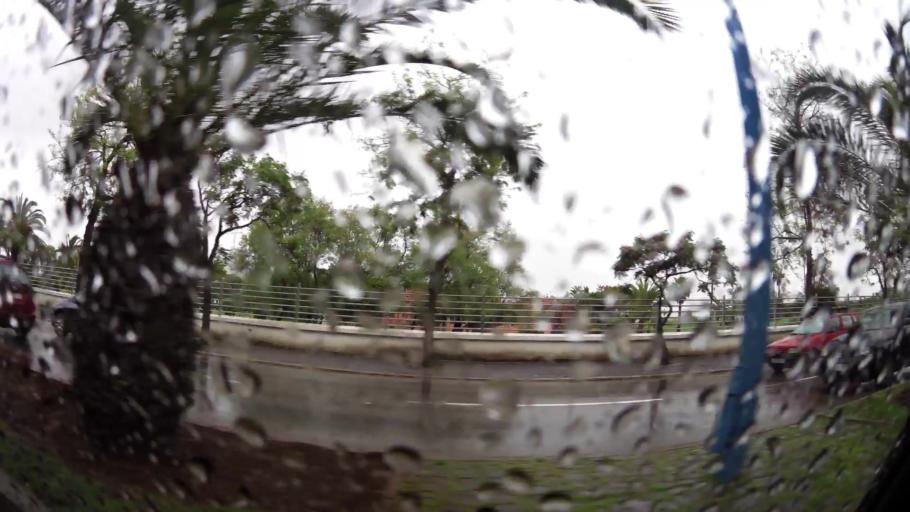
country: MA
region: Grand Casablanca
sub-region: Casablanca
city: Casablanca
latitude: 33.5606
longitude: -7.6694
